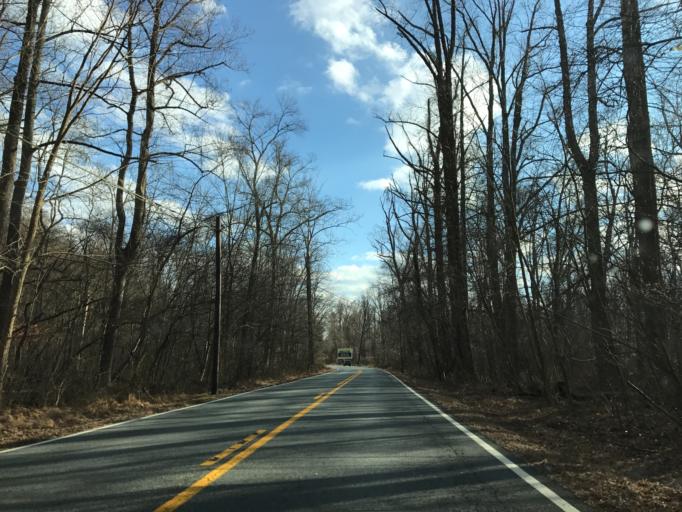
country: US
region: Maryland
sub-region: Harford County
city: Havre de Grace
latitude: 39.6361
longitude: -76.1486
